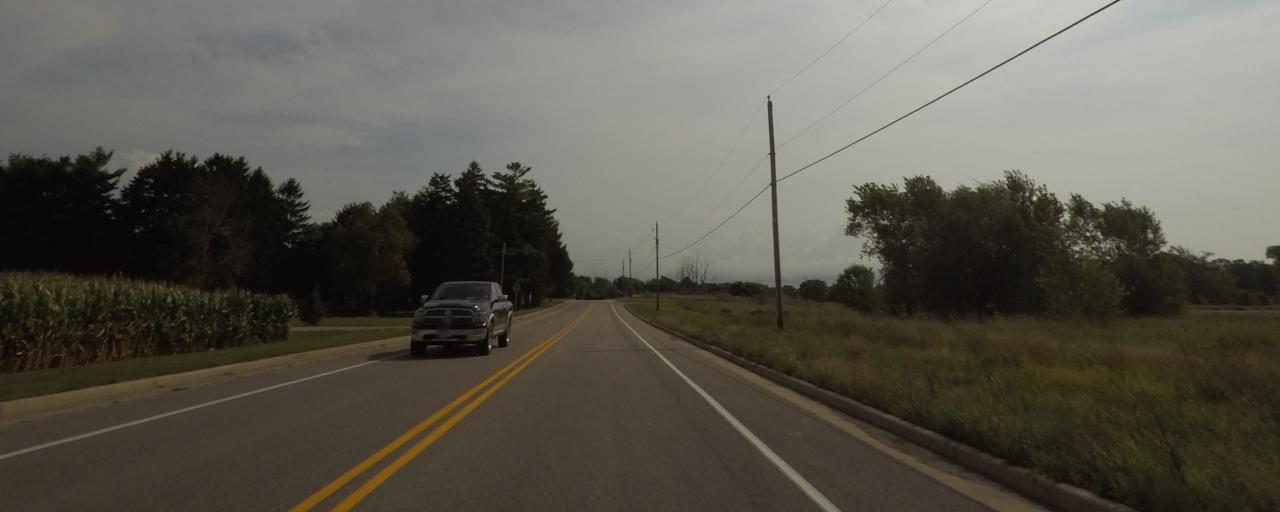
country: US
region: Wisconsin
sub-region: Jefferson County
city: Jefferson
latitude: 42.9942
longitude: -88.8314
